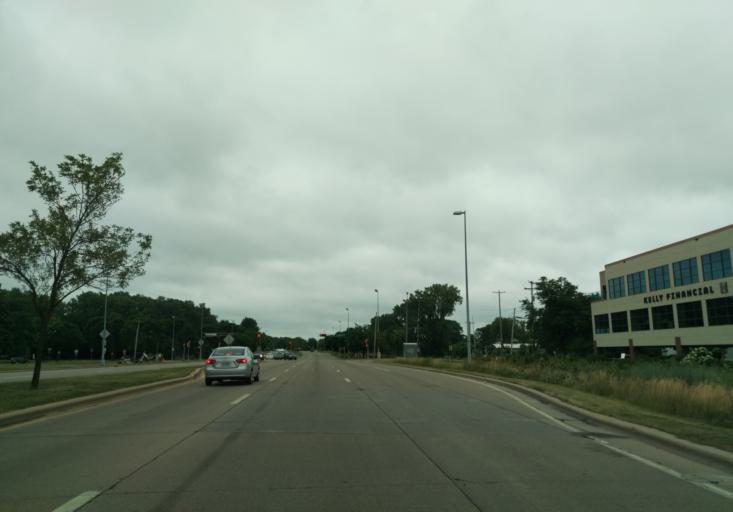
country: US
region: Wisconsin
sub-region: Dane County
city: Madison
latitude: 43.0569
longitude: -89.3829
